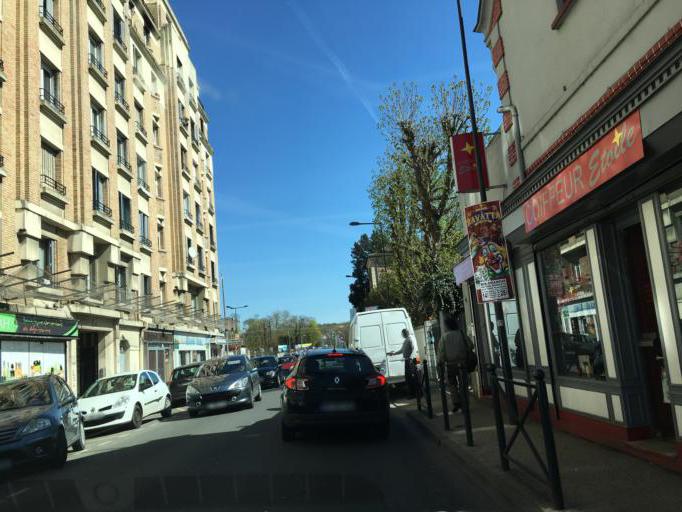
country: FR
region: Ile-de-France
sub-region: Departement de l'Essonne
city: Ris-Orangis
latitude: 48.6585
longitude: 2.4123
